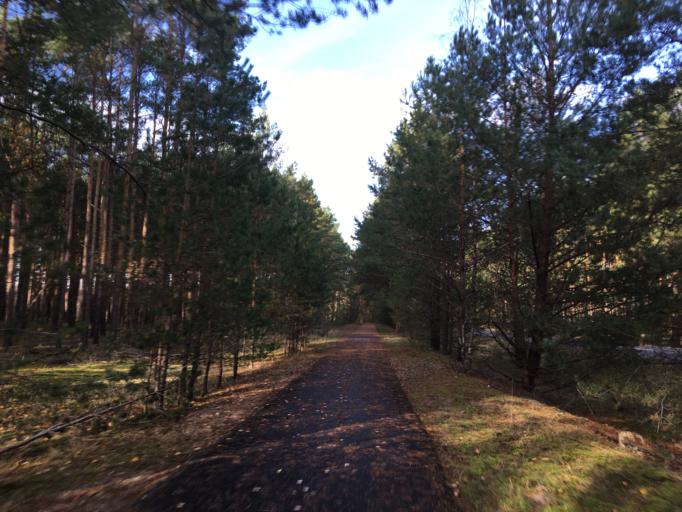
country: DE
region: Brandenburg
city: Gross Koris
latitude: 52.1586
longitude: 13.6712
